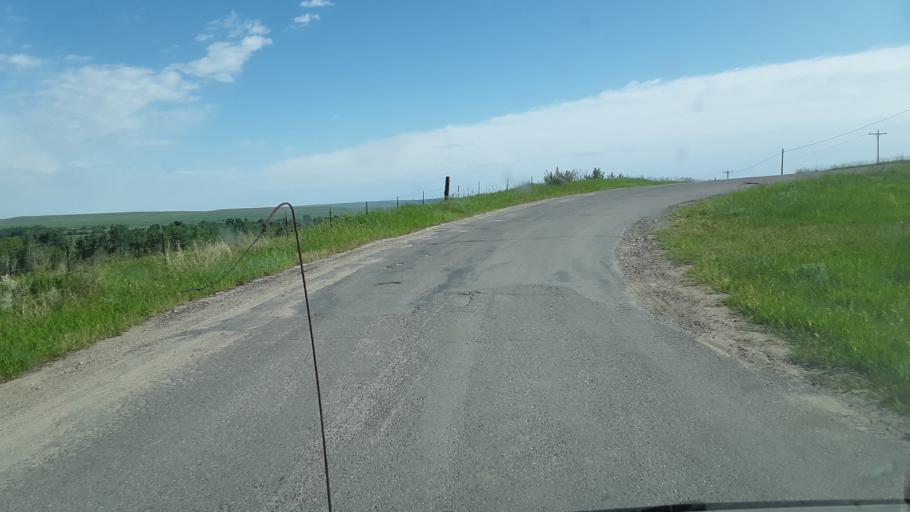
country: US
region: Montana
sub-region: Carbon County
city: Red Lodge
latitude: 45.3616
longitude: -109.1552
